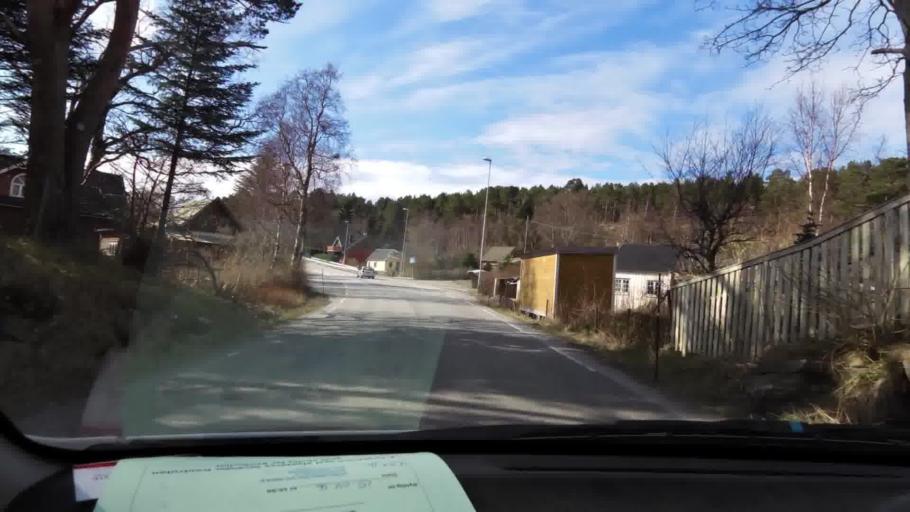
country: NO
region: More og Romsdal
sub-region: Kristiansund
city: Rensvik
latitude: 63.1082
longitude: 7.8210
